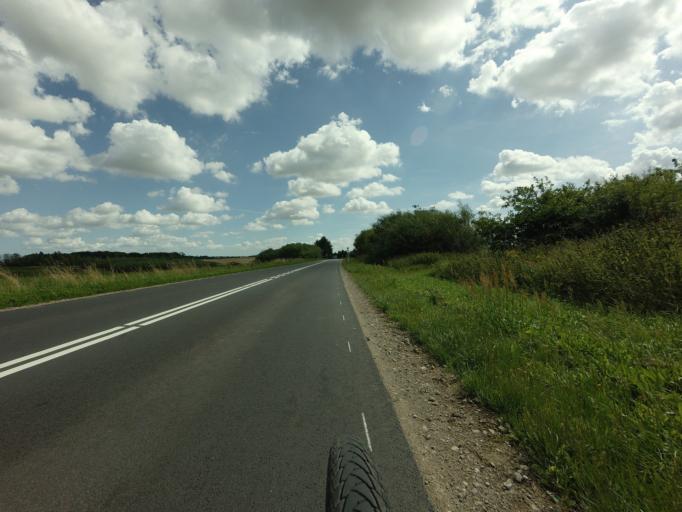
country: DK
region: North Denmark
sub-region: Hjorring Kommune
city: Hjorring
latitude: 57.4529
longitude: 9.9155
